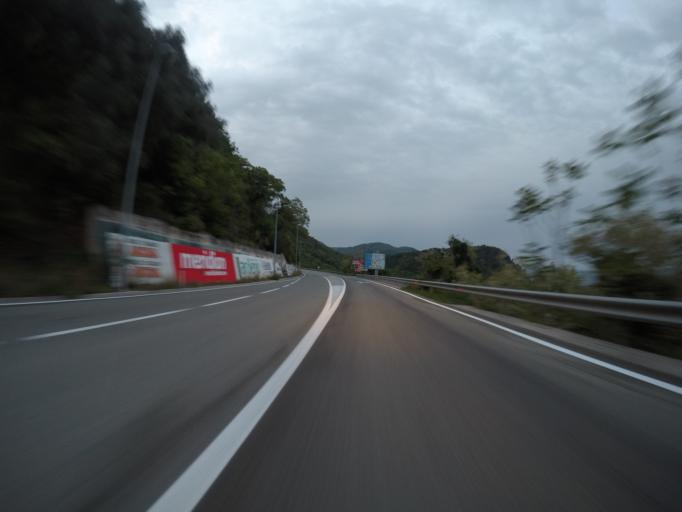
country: ME
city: Petrovac na Moru
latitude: 42.2049
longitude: 18.9504
